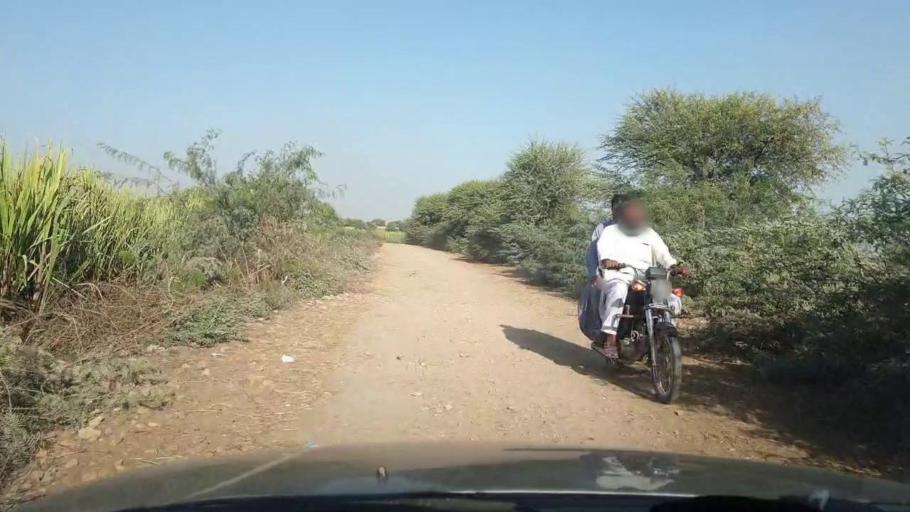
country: PK
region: Sindh
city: Bulri
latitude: 25.1109
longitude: 68.2691
